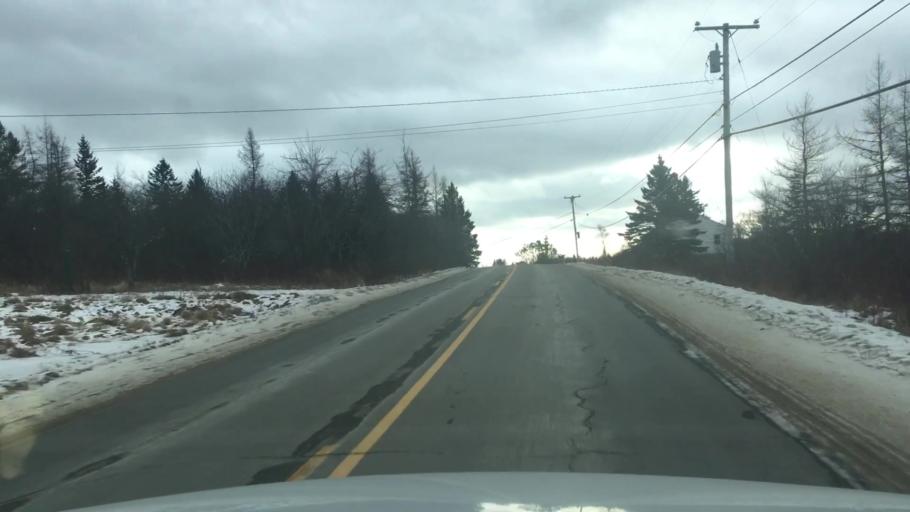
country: US
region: Maine
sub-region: Washington County
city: Machias
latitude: 44.6813
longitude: -67.4674
